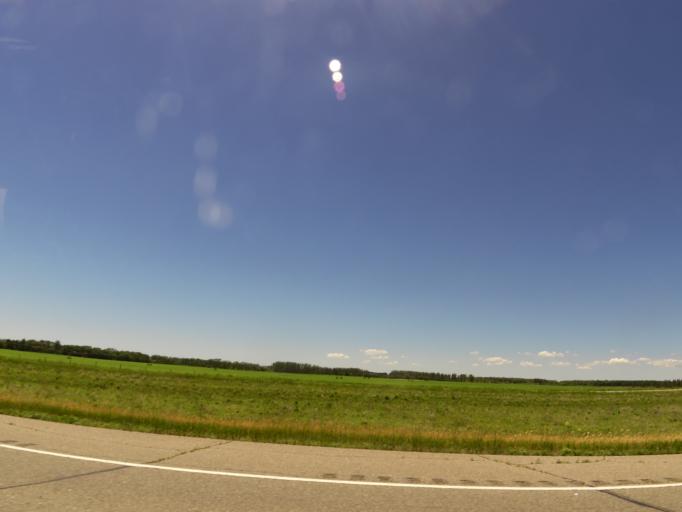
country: US
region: Minnesota
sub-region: Otter Tail County
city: Perham
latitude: 46.5993
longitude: -95.6037
